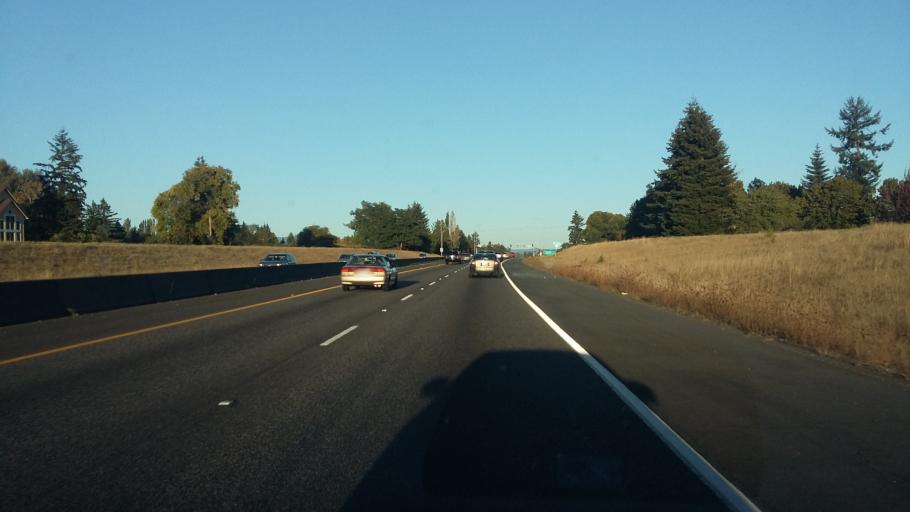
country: US
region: Washington
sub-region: Clark County
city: Minnehaha
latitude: 45.6477
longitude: -122.6221
